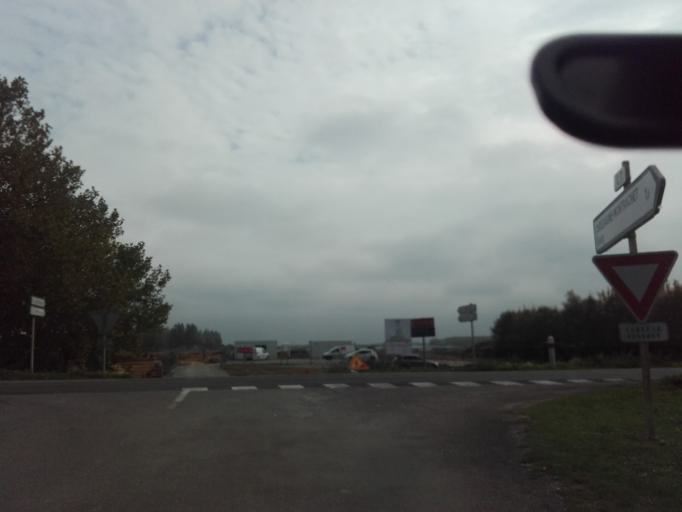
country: FR
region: Bourgogne
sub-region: Departement de la Cote-d'Or
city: Corpeau
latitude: 46.9242
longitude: 4.7377
